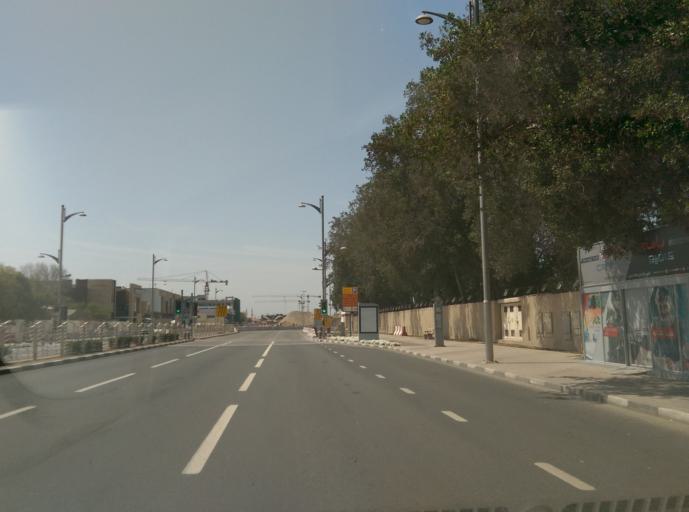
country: AE
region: Dubai
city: Dubai
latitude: 25.2006
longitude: 55.2394
